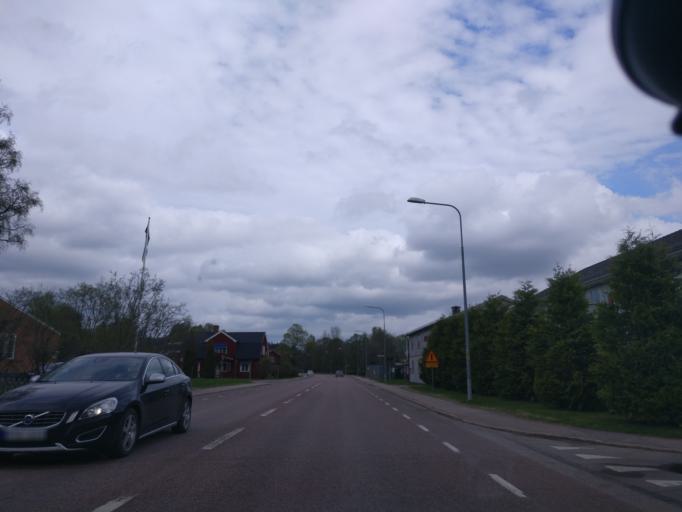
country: SE
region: Vaermland
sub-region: Hagfors Kommun
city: Ekshaerad
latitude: 60.1777
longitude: 13.4960
